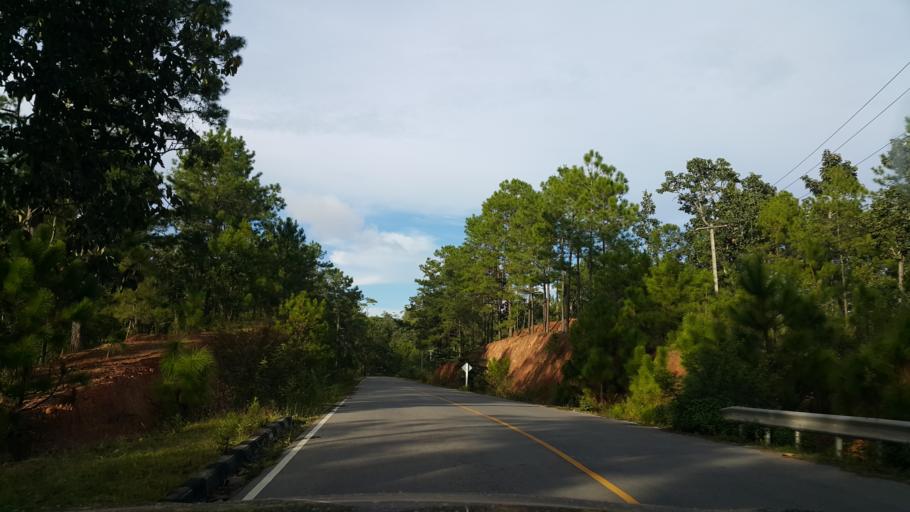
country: TH
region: Chiang Mai
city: Chaem Luang
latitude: 19.0932
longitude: 98.3427
